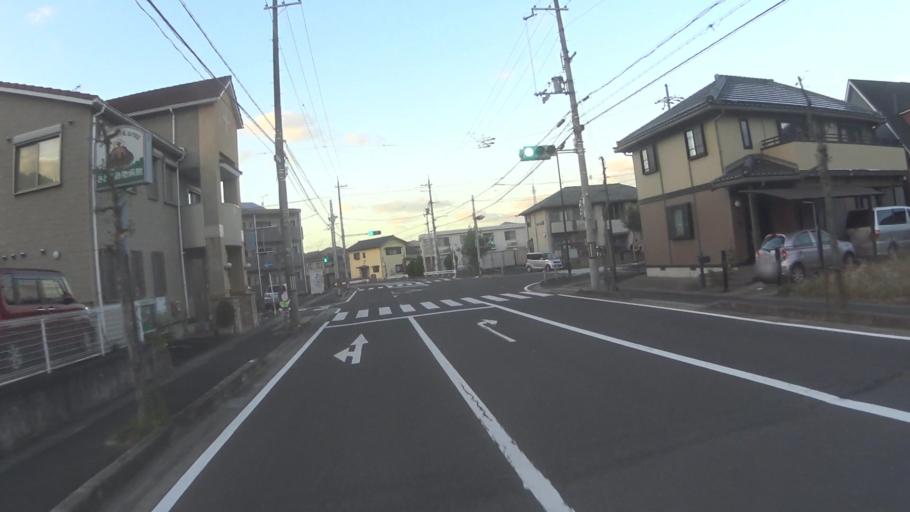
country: JP
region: Kyoto
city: Ayabe
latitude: 35.2989
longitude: 135.2346
